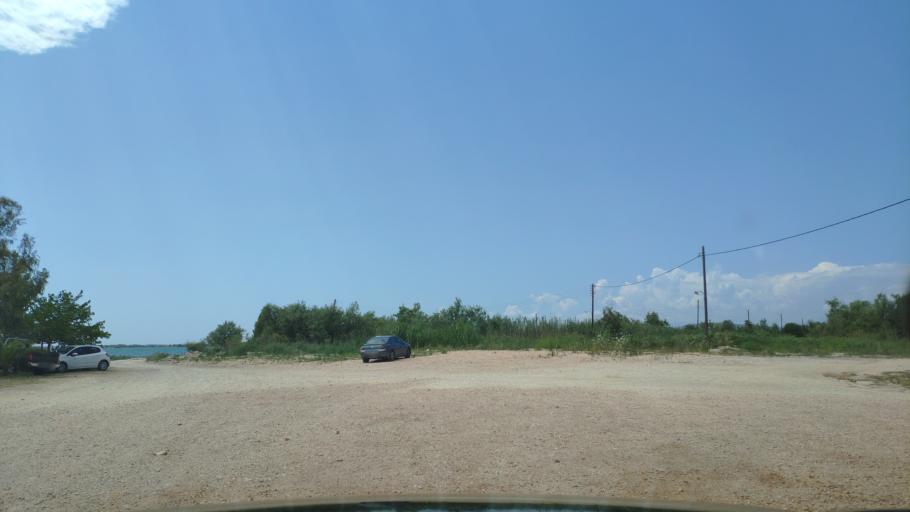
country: GR
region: West Greece
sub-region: Nomos Aitolias kai Akarnanias
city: Menidi
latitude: 39.0473
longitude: 21.1074
